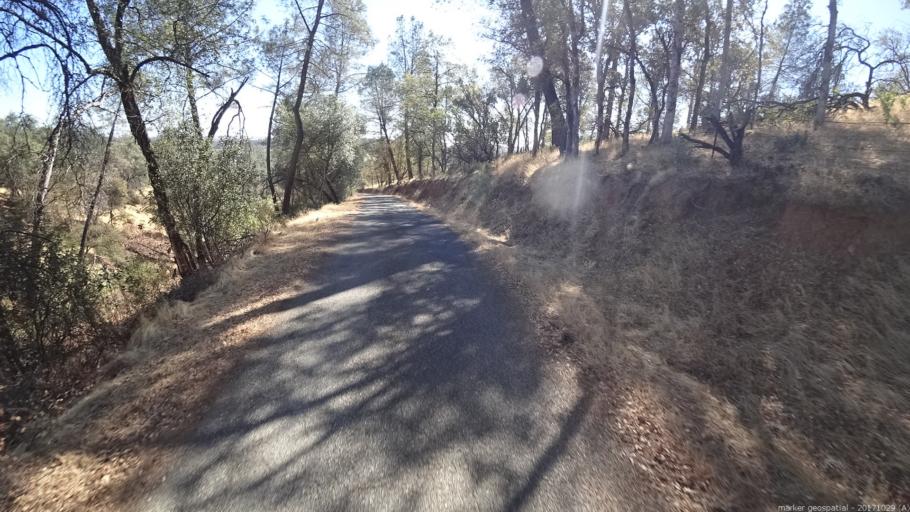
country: US
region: California
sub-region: Shasta County
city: Shasta
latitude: 40.4791
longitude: -122.6240
